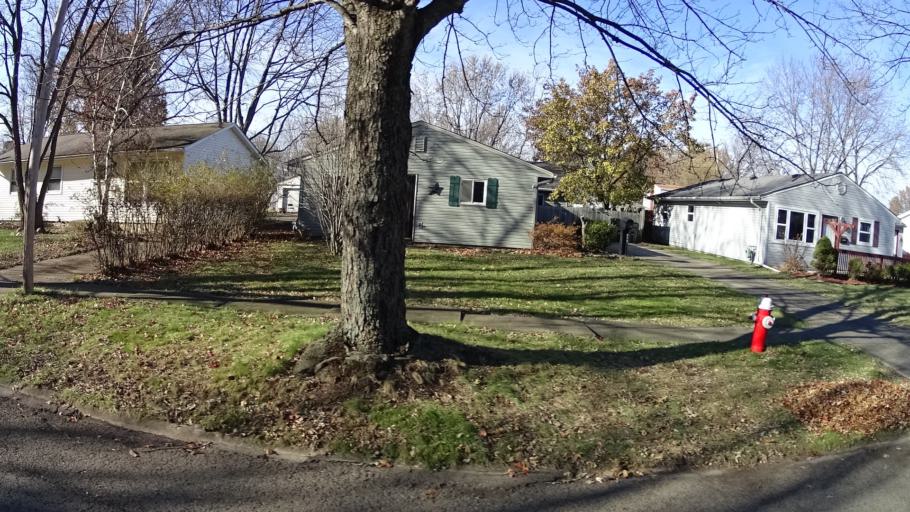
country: US
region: Ohio
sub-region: Lorain County
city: Sheffield
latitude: 41.3983
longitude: -82.0693
